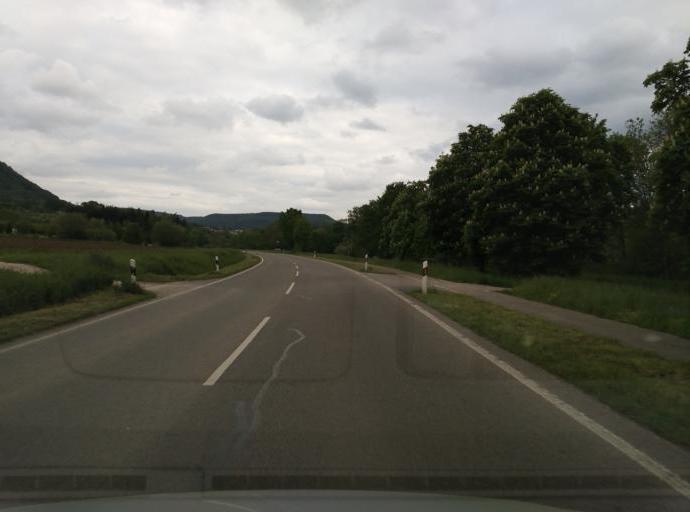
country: DE
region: Baden-Wuerttemberg
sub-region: Regierungsbezirk Stuttgart
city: Neuffen
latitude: 48.5733
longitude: 9.3736
